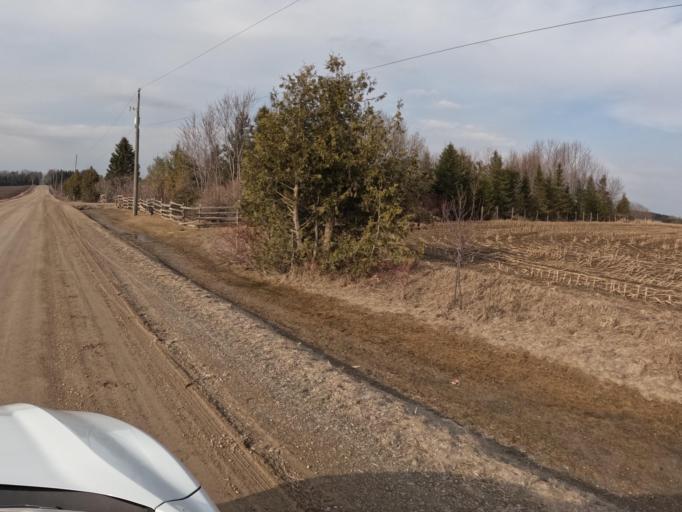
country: CA
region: Ontario
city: Orangeville
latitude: 43.9051
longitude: -80.2689
